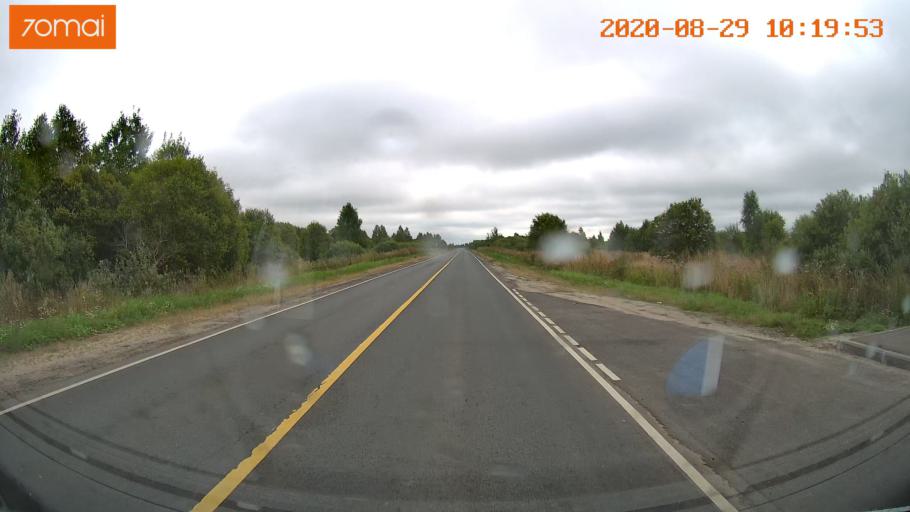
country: RU
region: Ivanovo
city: Yur'yevets
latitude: 57.3261
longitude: 42.8706
